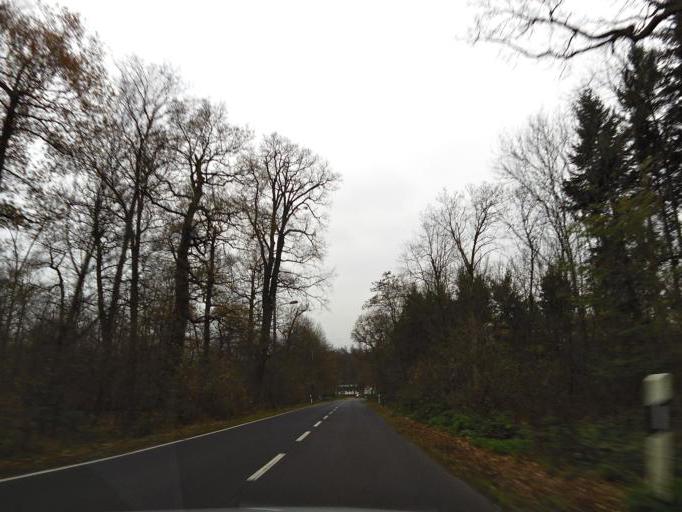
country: DE
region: Hesse
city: Kelsterbach
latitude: 50.0755
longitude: 8.5777
